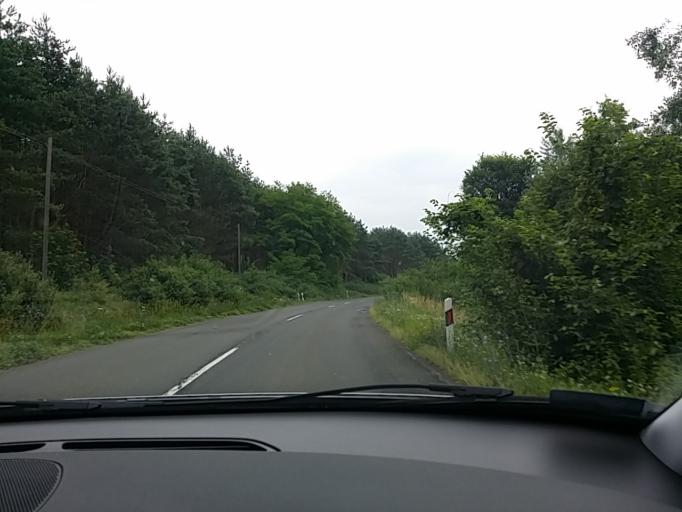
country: HU
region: Nograd
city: Matraterenye
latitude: 48.0098
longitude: 19.9631
